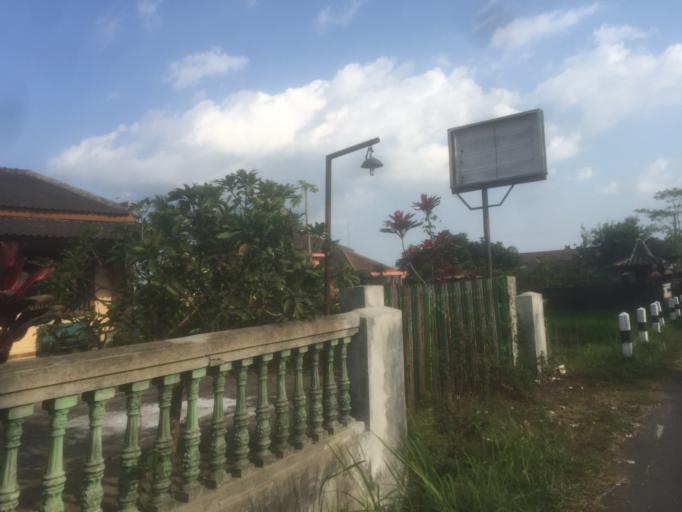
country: ID
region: Daerah Istimewa Yogyakarta
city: Sleman
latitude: -7.6470
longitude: 110.4243
